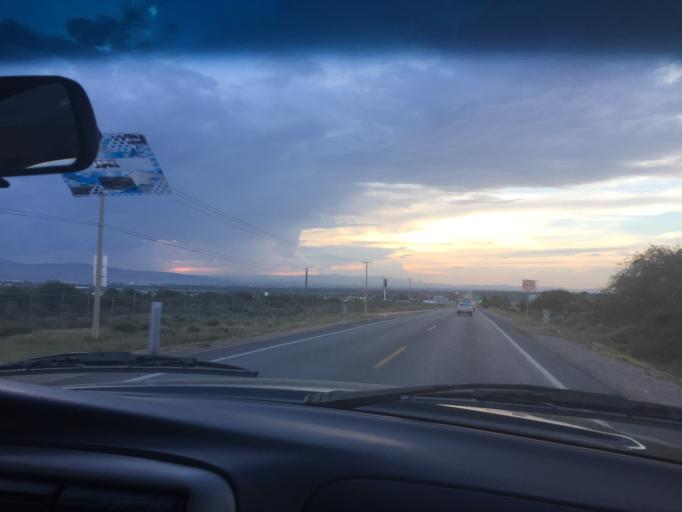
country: MX
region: San Luis Potosi
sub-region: San Luis Potosi
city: Ciudad Satelite
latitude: 22.1260
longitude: -100.8192
